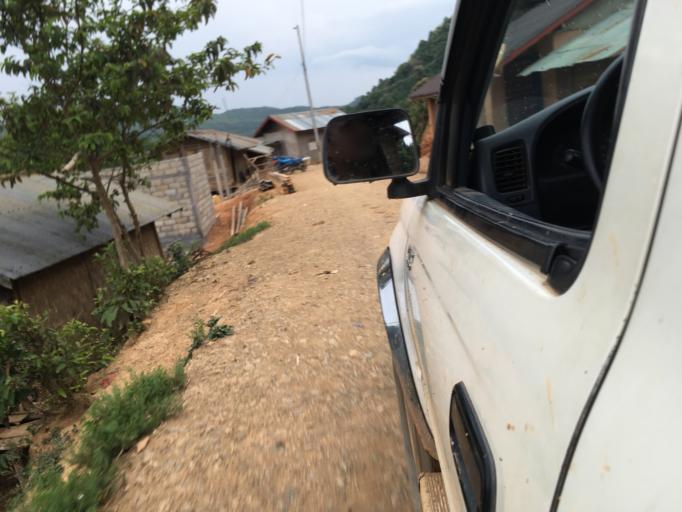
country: LA
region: Oudomxai
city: Muang La
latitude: 20.8922
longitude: 102.3423
